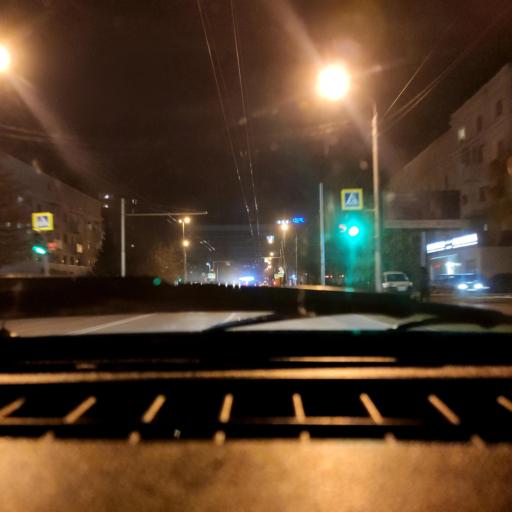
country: RU
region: Bashkortostan
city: Ufa
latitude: 54.7850
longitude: 56.1314
